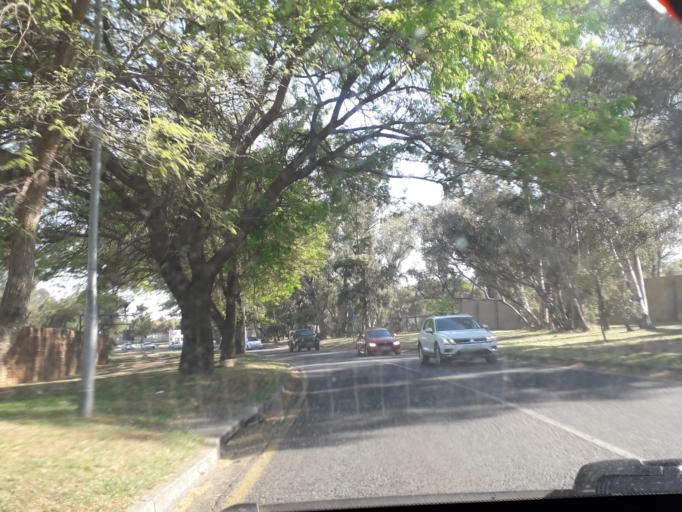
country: ZA
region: Gauteng
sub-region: City of Johannesburg Metropolitan Municipality
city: Midrand
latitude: -26.0504
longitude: 28.0718
